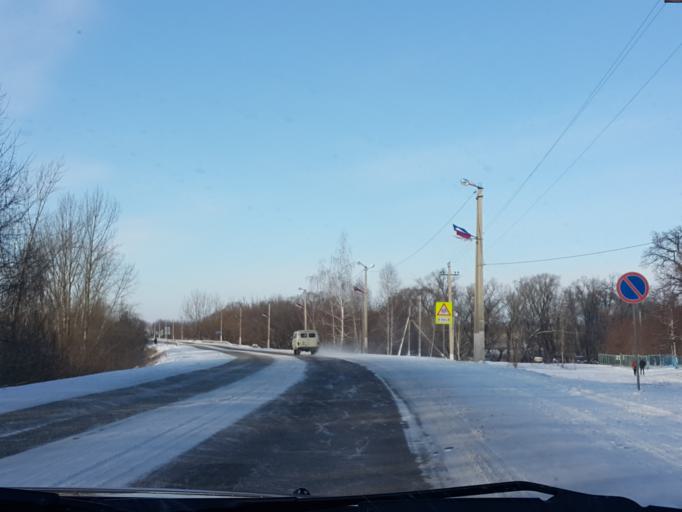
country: RU
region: Tambov
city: Znamenka
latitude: 52.4171
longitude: 41.4378
